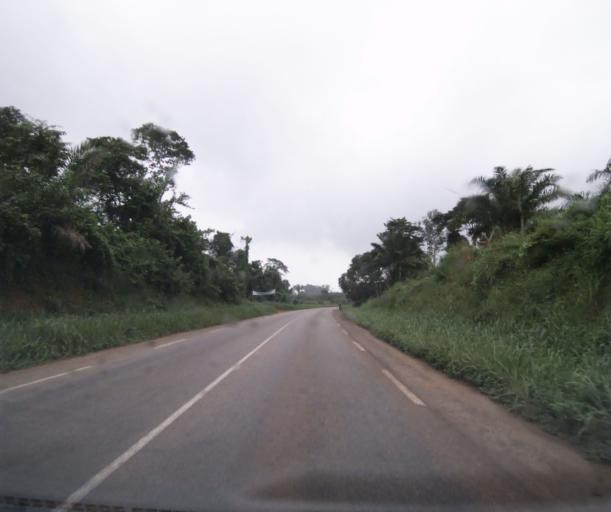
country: CM
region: Centre
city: Eseka
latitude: 3.8696
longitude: 10.6549
